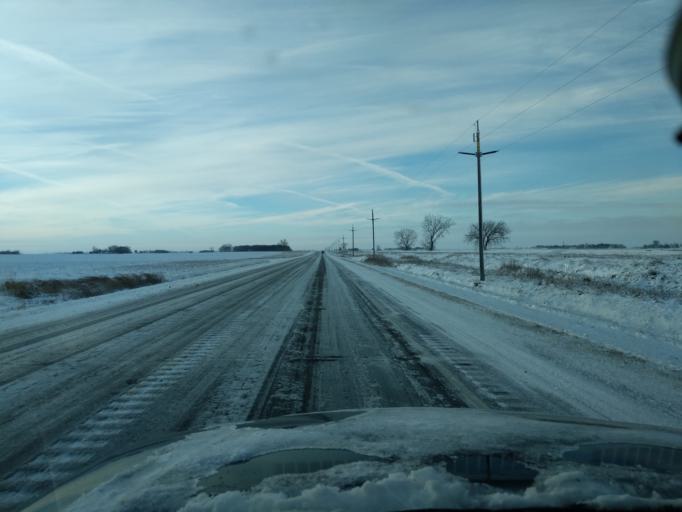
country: US
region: Minnesota
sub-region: Renville County
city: Hector
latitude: 44.7479
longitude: -94.7413
